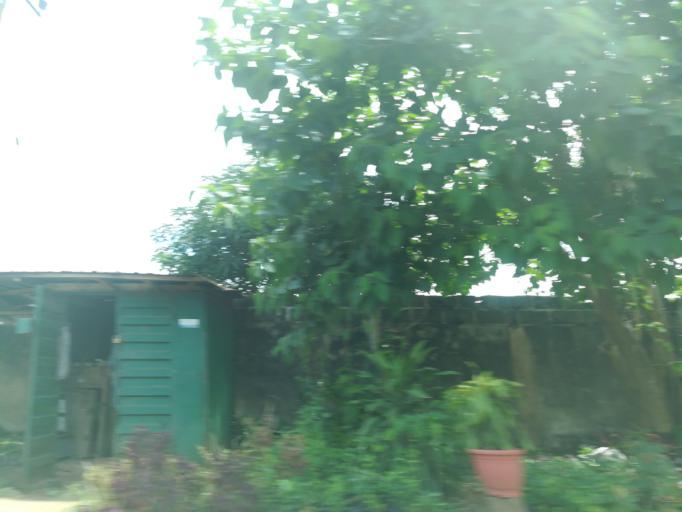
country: NG
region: Lagos
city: Ebute Ikorodu
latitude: 6.5986
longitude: 3.4960
